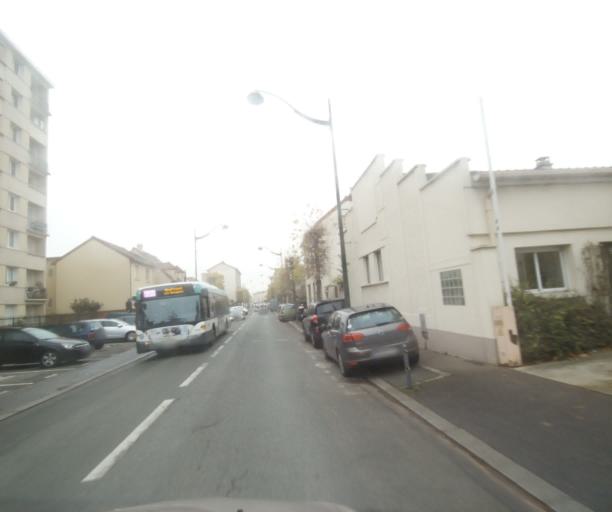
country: FR
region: Ile-de-France
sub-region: Departement de Seine-Saint-Denis
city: Les Pavillons-sous-Bois
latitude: 48.9069
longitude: 2.4980
